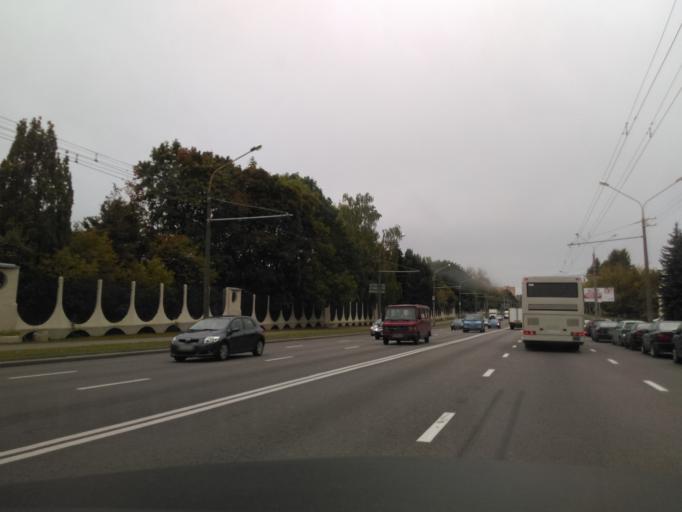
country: BY
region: Minsk
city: Minsk
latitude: 53.9138
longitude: 27.6051
